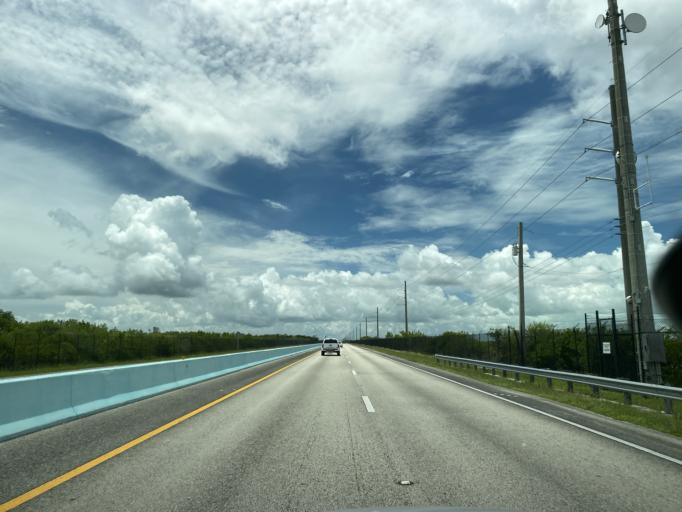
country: US
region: Florida
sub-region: Miami-Dade County
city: Florida City
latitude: 25.3550
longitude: -80.4591
